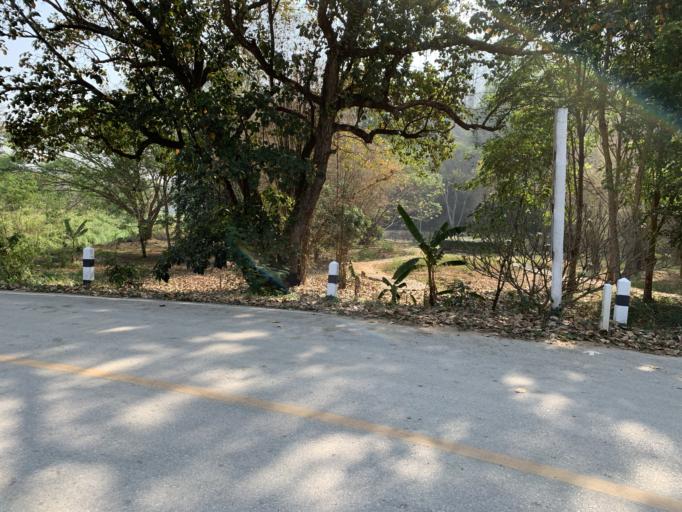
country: TH
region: Lampang
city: Hang Chat
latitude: 18.3582
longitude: 99.2557
